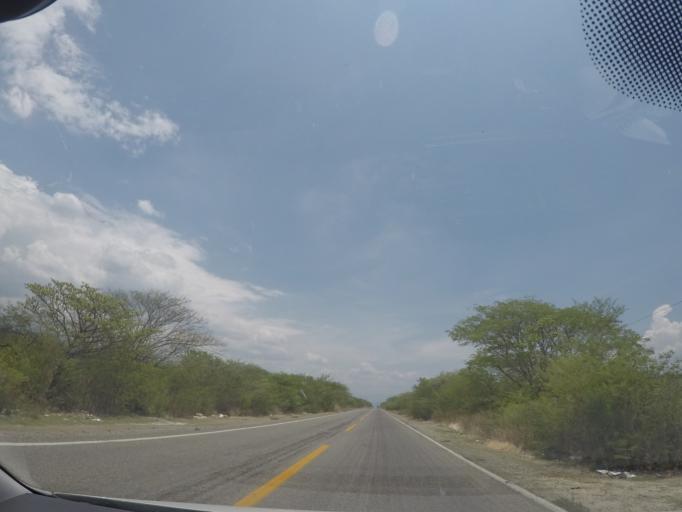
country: MX
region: Oaxaca
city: Magdalena Tequisistlan
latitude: 16.4224
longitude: -95.5474
